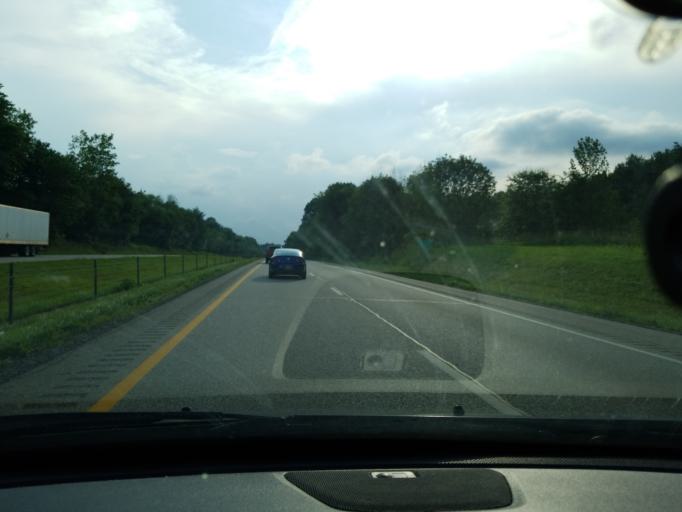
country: US
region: Ohio
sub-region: Portage County
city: Brimfield
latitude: 41.1095
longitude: -81.2905
